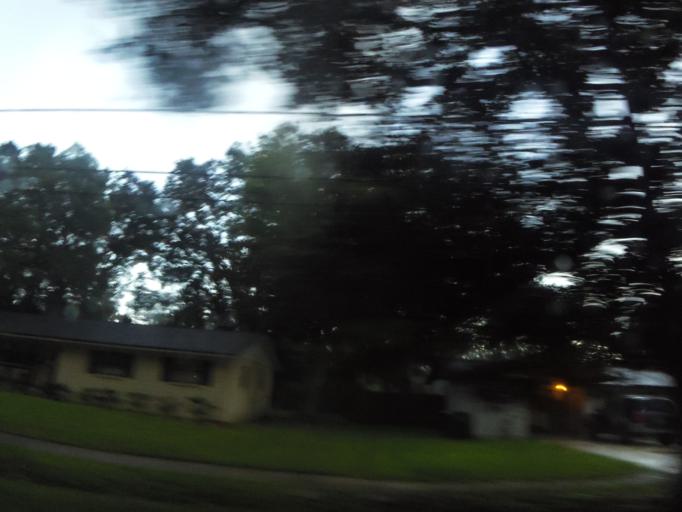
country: US
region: Florida
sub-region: Duval County
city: Jacksonville
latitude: 30.2468
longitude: -81.6182
